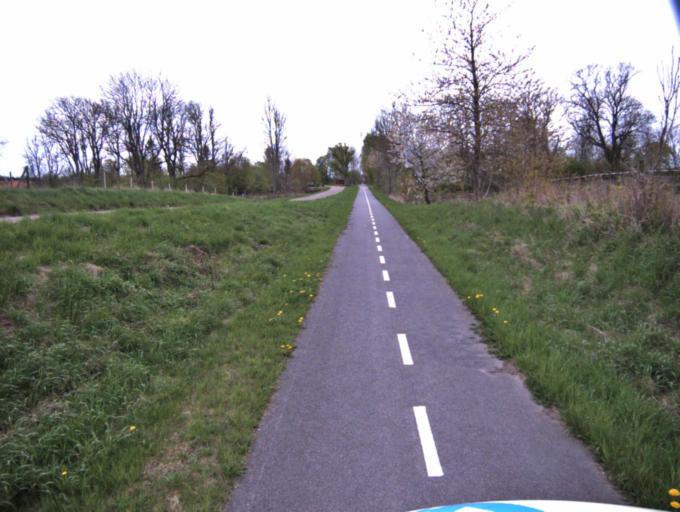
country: SE
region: Skane
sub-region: Kristianstads Kommun
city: Onnestad
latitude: 55.9910
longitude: 14.0334
